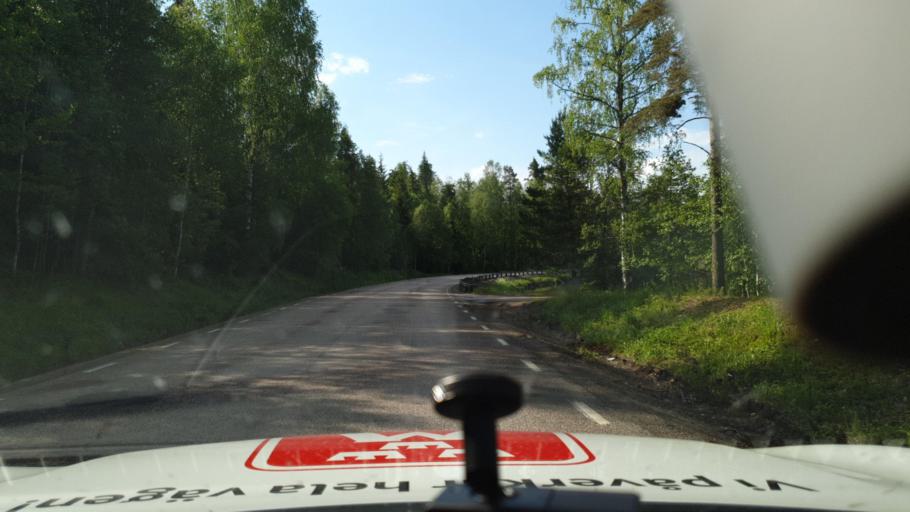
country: SE
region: Vaermland
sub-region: Arvika Kommun
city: Arvika
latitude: 59.9192
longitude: 12.6553
